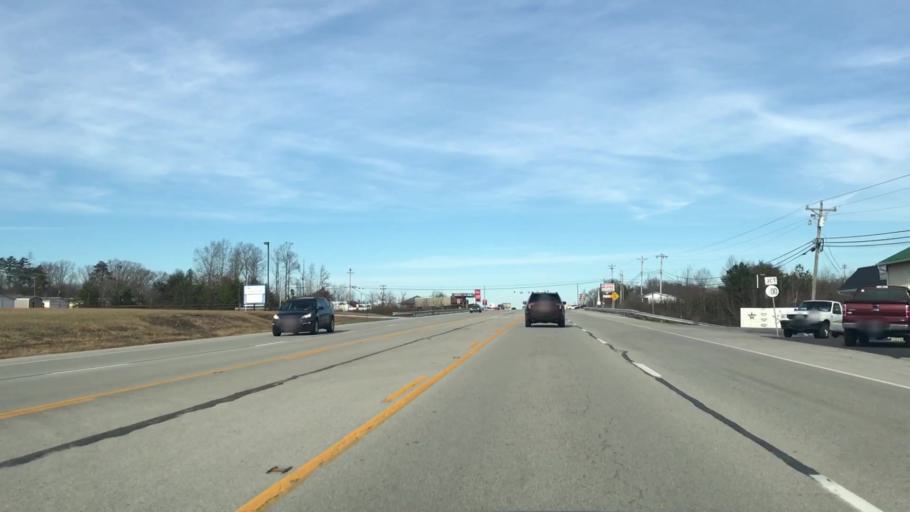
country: US
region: Kentucky
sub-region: McCreary County
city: Whitley City
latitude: 36.7444
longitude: -84.4732
